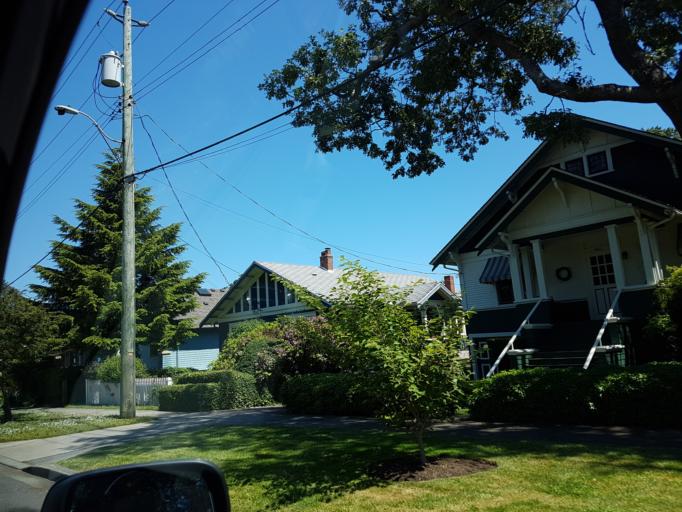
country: CA
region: British Columbia
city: Oak Bay
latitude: 48.4273
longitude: -123.3275
